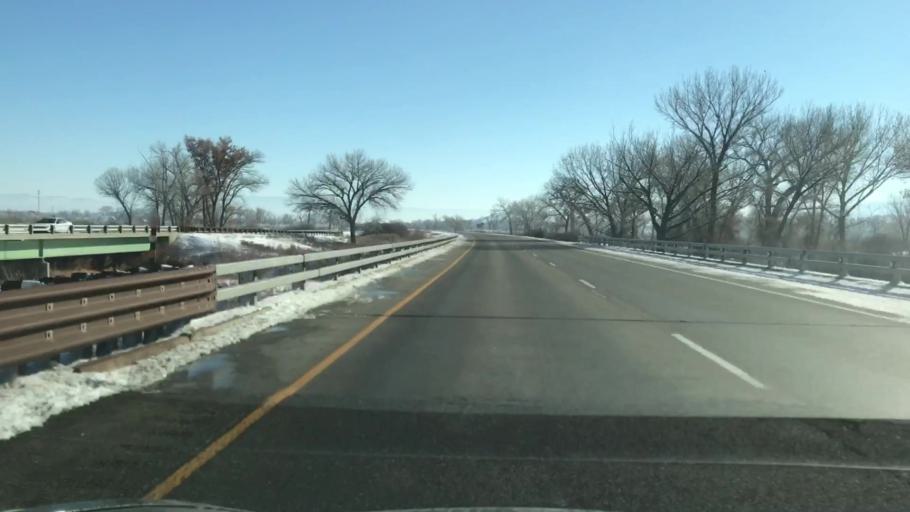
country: US
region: Colorado
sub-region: Mesa County
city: Loma
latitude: 39.1656
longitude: -108.7858
